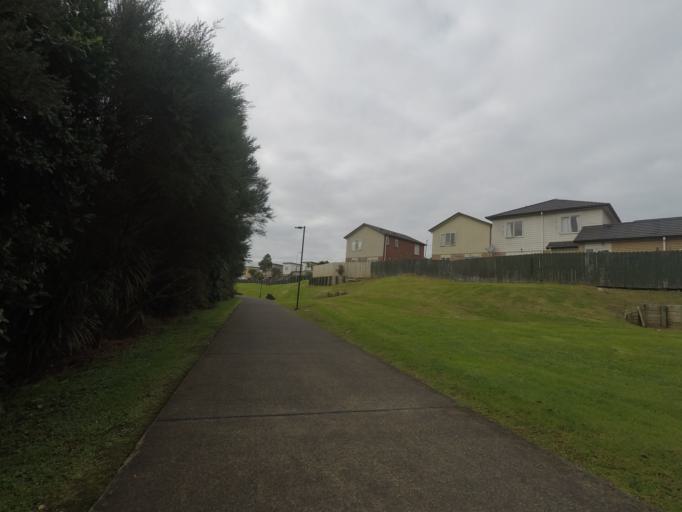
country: NZ
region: Auckland
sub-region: Auckland
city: Waitakere
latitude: -36.8998
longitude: 174.6277
